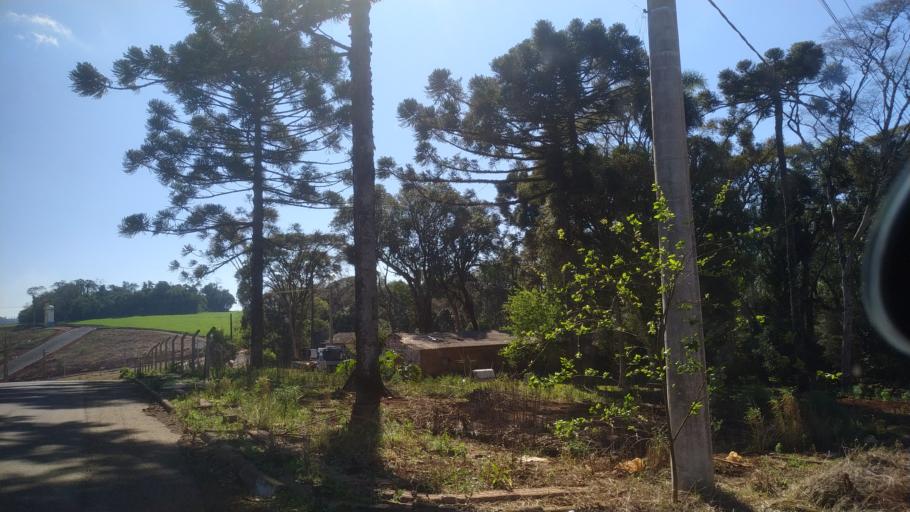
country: BR
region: Santa Catarina
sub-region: Chapeco
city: Chapeco
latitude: -27.0873
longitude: -52.6922
